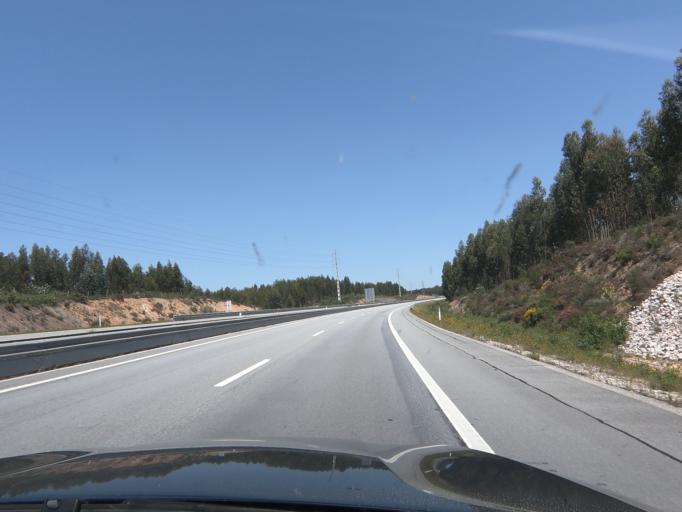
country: PT
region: Santarem
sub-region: Entroncamento
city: Entroncamento
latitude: 39.5000
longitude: -8.4365
